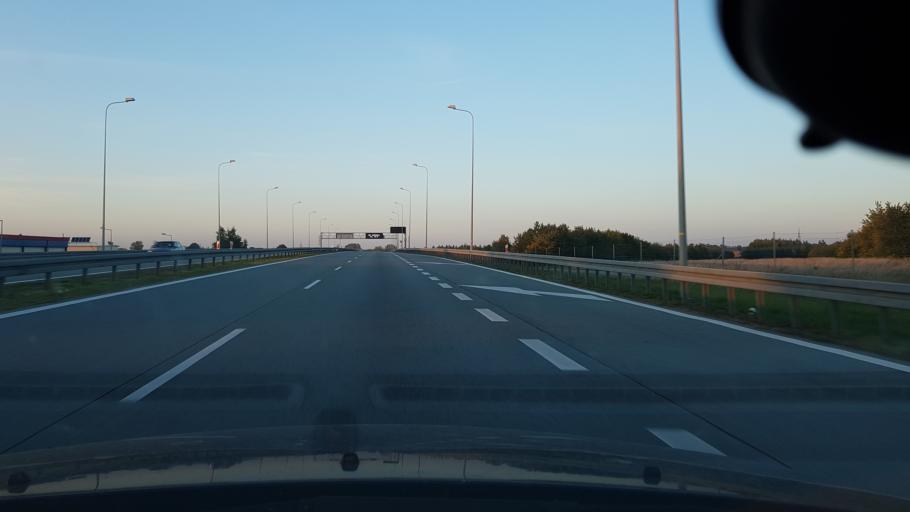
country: PL
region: Lodz Voivodeship
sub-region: Powiat rawski
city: Rawa Mazowiecka
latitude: 51.7744
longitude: 20.2747
